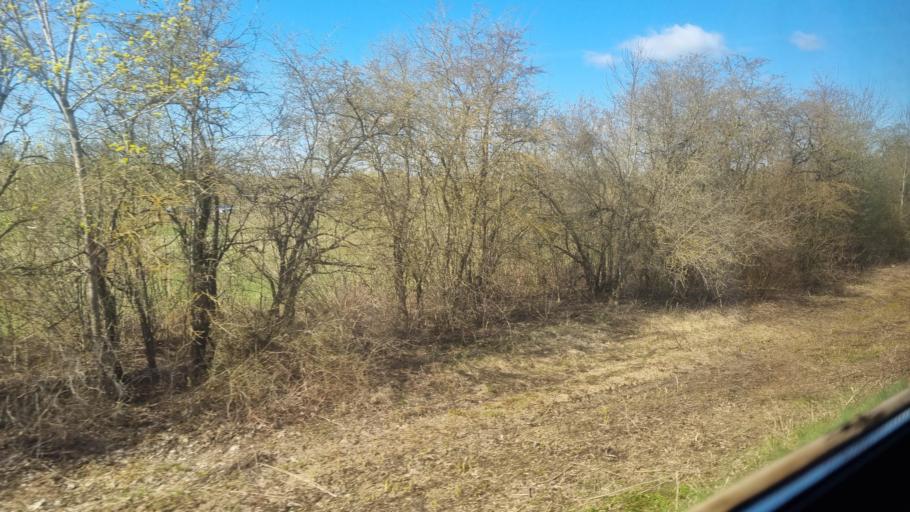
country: LV
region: Lielvarde
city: Lielvarde
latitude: 56.7164
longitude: 24.8427
